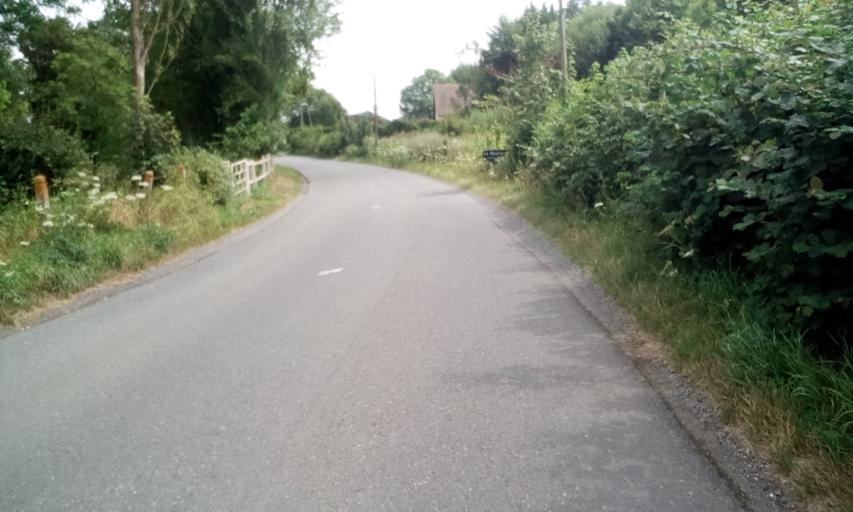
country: FR
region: Lower Normandy
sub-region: Departement du Calvados
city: Bavent
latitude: 49.2467
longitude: -0.1870
